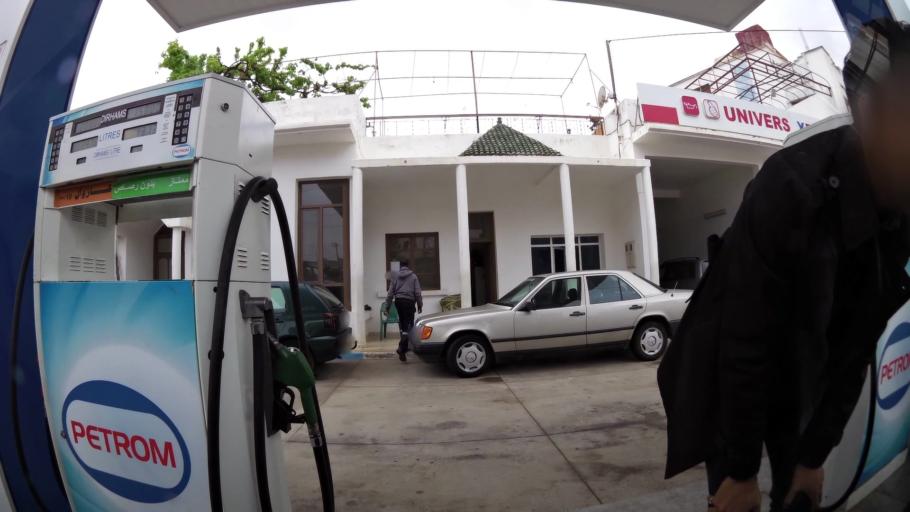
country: MA
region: Oriental
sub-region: Nador
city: Midar
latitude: 35.0480
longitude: -3.4571
